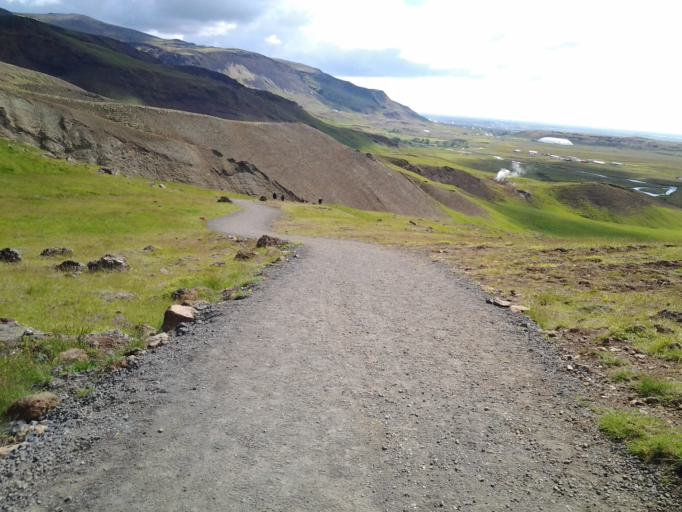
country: IS
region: South
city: Hveragerdi
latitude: 64.0281
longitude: -21.2119
